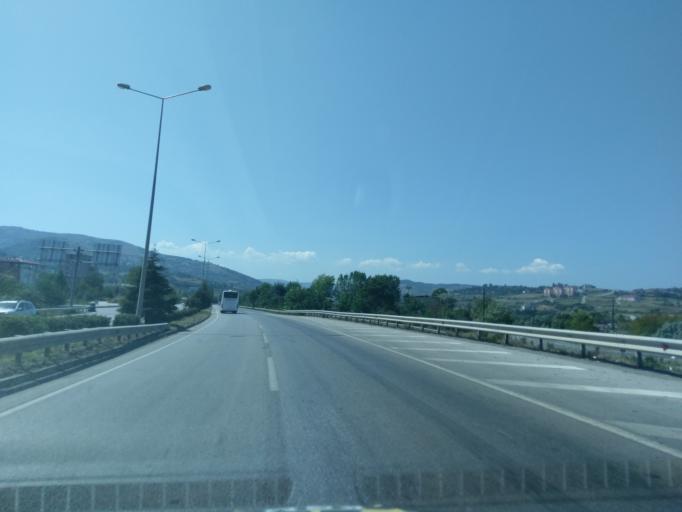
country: TR
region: Samsun
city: Samsun
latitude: 41.2544
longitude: 36.3187
